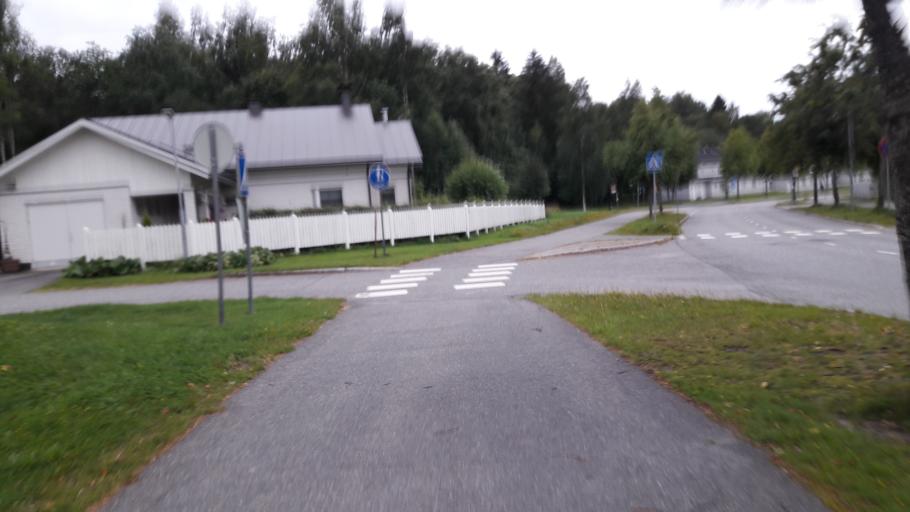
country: FI
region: North Karelia
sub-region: Joensuu
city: Joensuu
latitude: 62.6181
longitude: 29.6957
